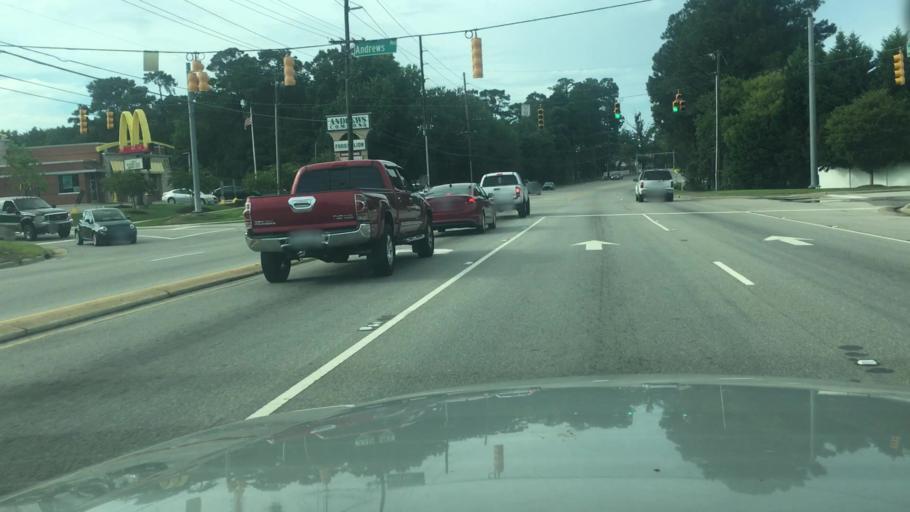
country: US
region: North Carolina
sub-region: Cumberland County
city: Eastover
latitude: 35.1571
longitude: -78.8693
